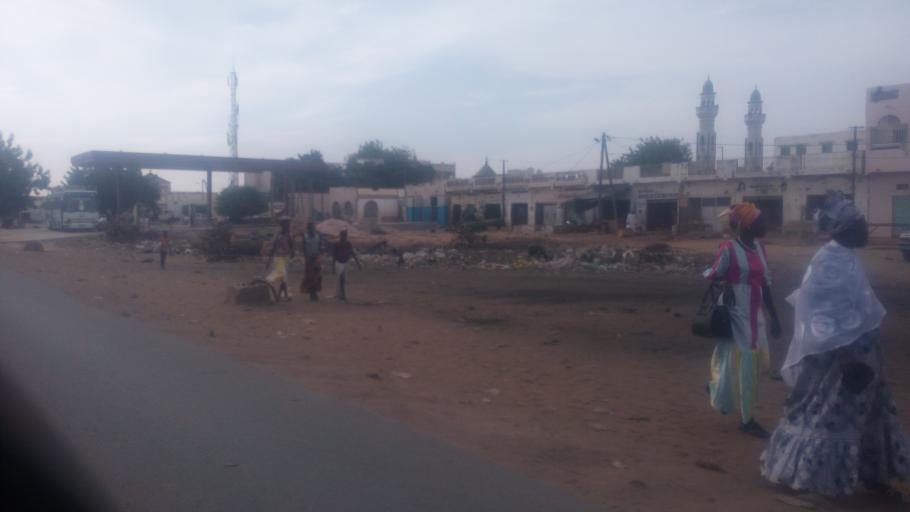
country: SN
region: Diourbel
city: Touba
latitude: 14.8804
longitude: -15.8946
